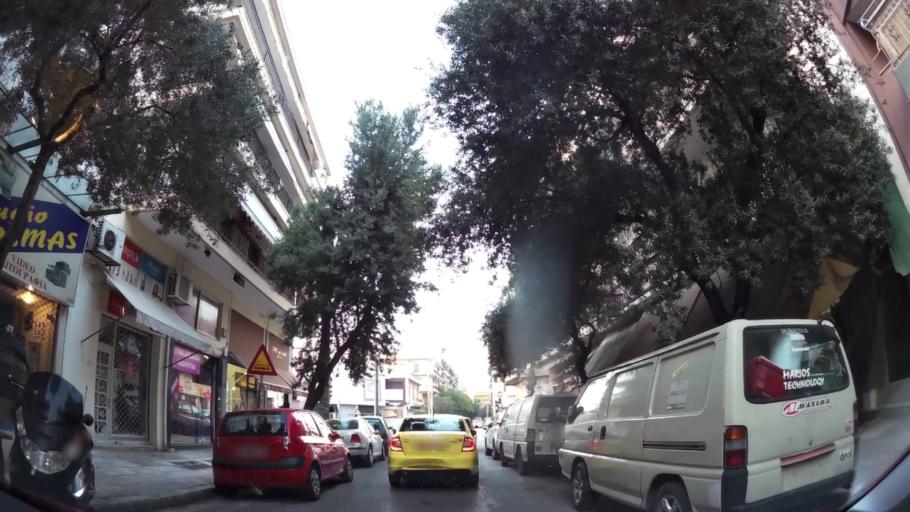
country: GR
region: Attica
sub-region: Nomarchia Athinas
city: Dhafni
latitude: 37.9559
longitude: 23.7262
